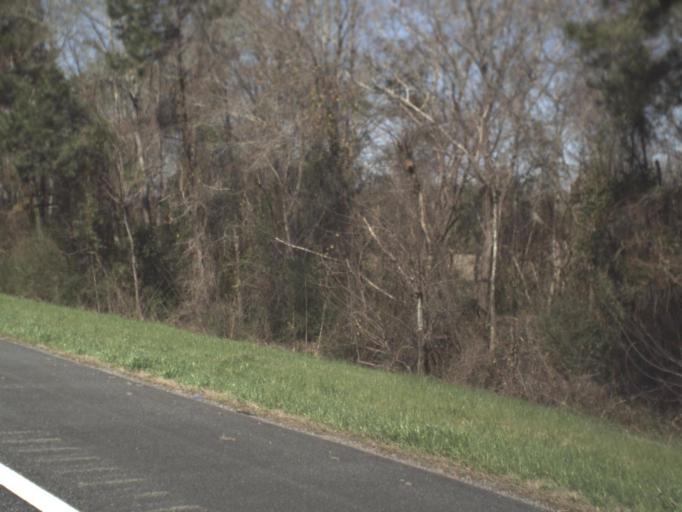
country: US
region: Florida
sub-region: Jackson County
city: Marianna
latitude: 30.7559
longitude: -85.3551
